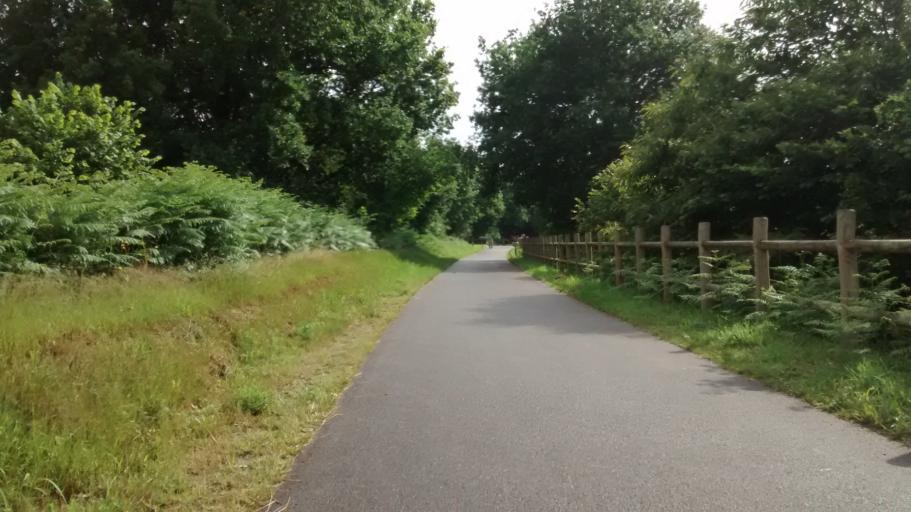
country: FR
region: Brittany
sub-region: Departement du Morbihan
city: Pleucadeuc
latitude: 47.7803
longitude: -2.3908
